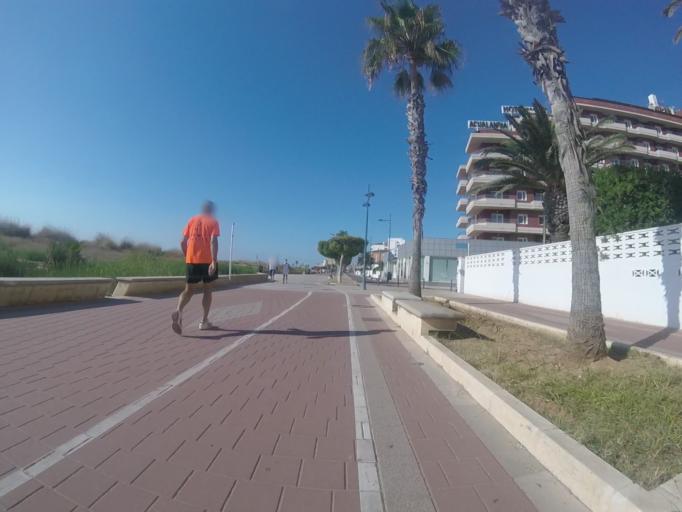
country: ES
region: Valencia
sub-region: Provincia de Castello
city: Peniscola
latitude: 40.3863
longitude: 0.4102
